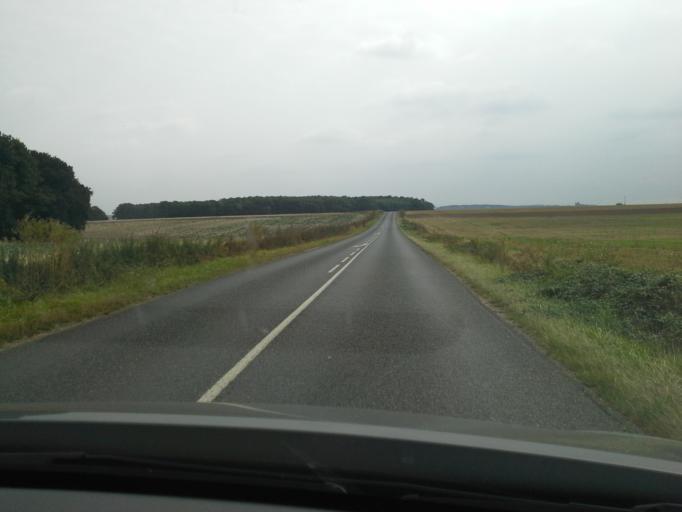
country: FR
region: Centre
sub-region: Departement du Loir-et-Cher
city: Vendome
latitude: 47.7508
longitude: 1.0772
